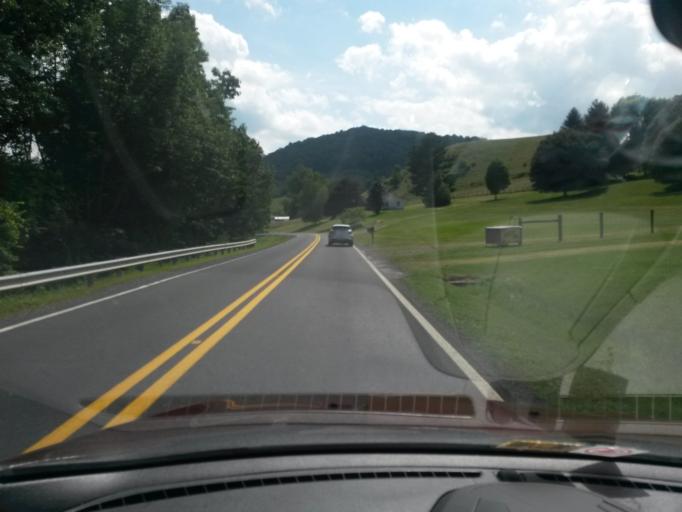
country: US
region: West Virginia
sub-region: Pendleton County
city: Franklin
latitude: 38.5499
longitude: -79.4438
